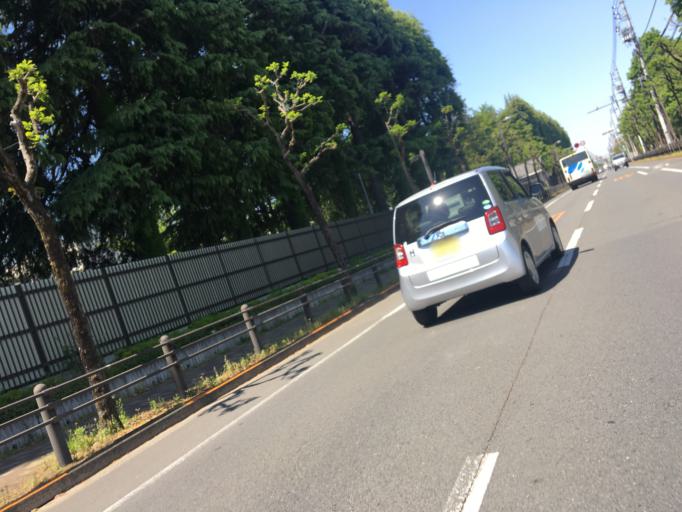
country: JP
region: Tokyo
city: Kokubunji
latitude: 35.7193
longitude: 139.4882
